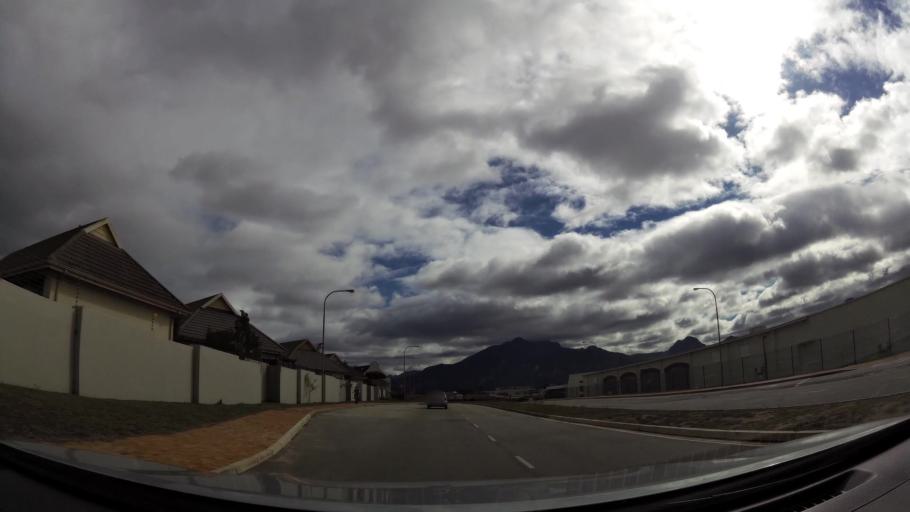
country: ZA
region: Western Cape
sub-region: Eden District Municipality
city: George
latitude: -33.9841
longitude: 22.4979
